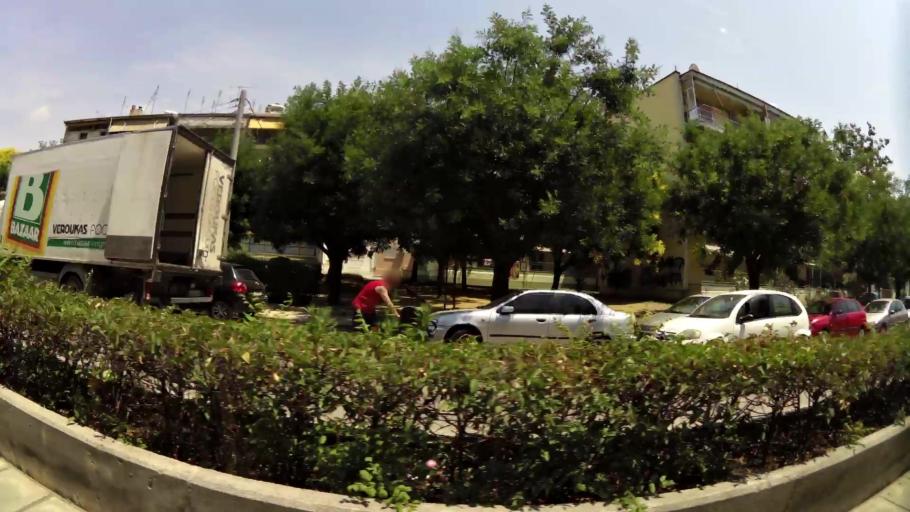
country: GR
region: Central Macedonia
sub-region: Nomos Thessalonikis
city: Thessaloniki
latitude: 40.6467
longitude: 22.9316
